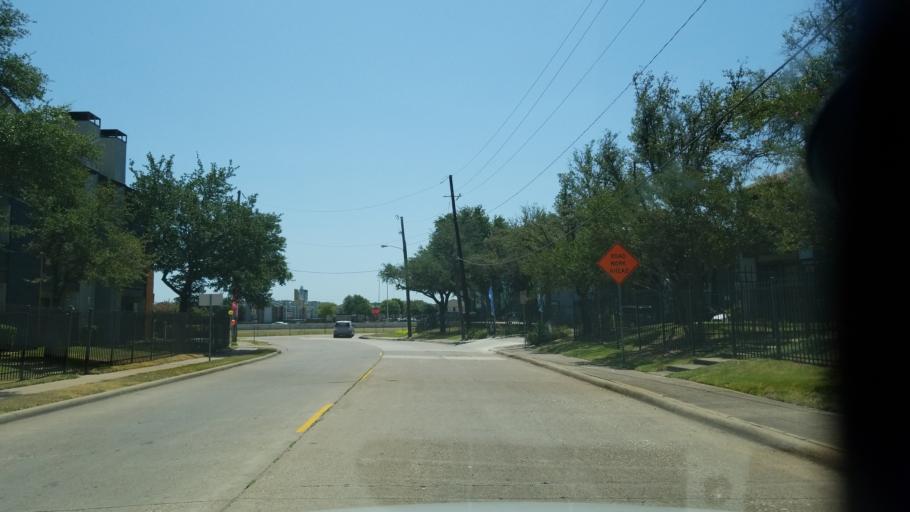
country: US
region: Texas
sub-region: Dallas County
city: Duncanville
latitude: 32.6524
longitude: -96.8822
